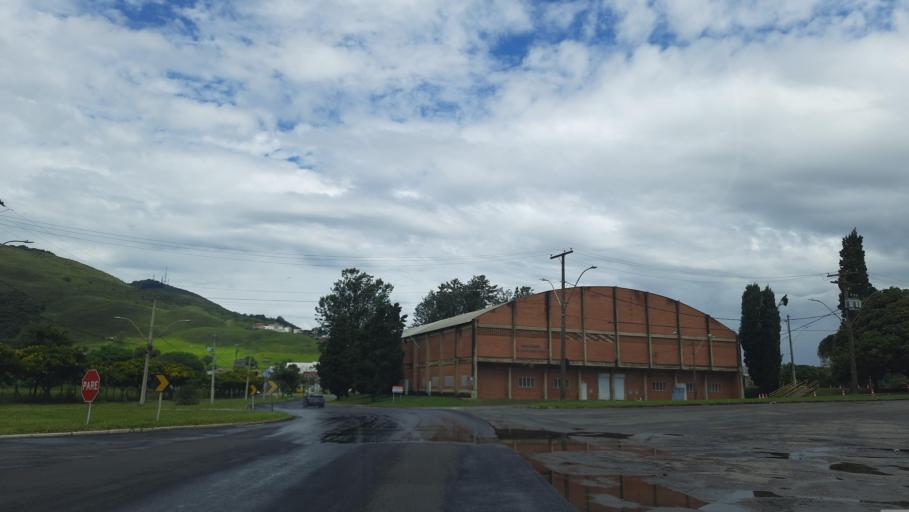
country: BR
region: Minas Gerais
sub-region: Pocos De Caldas
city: Pocos de Caldas
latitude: -21.7759
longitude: -46.6063
